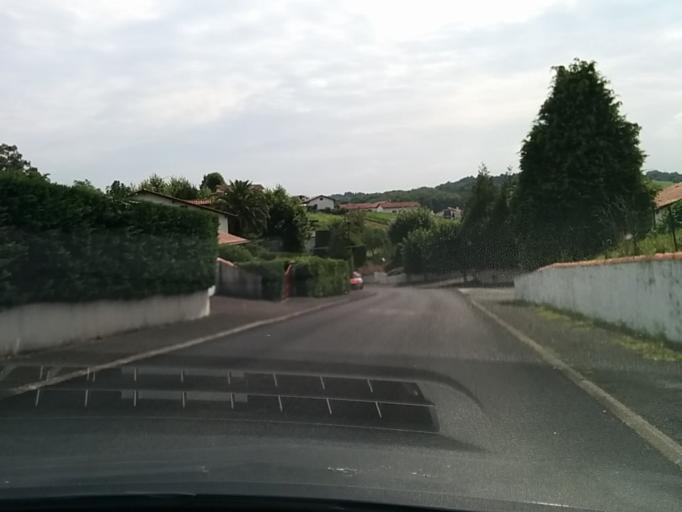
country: FR
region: Aquitaine
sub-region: Departement des Pyrenees-Atlantiques
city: Urrugne
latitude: 43.3657
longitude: -1.7005
